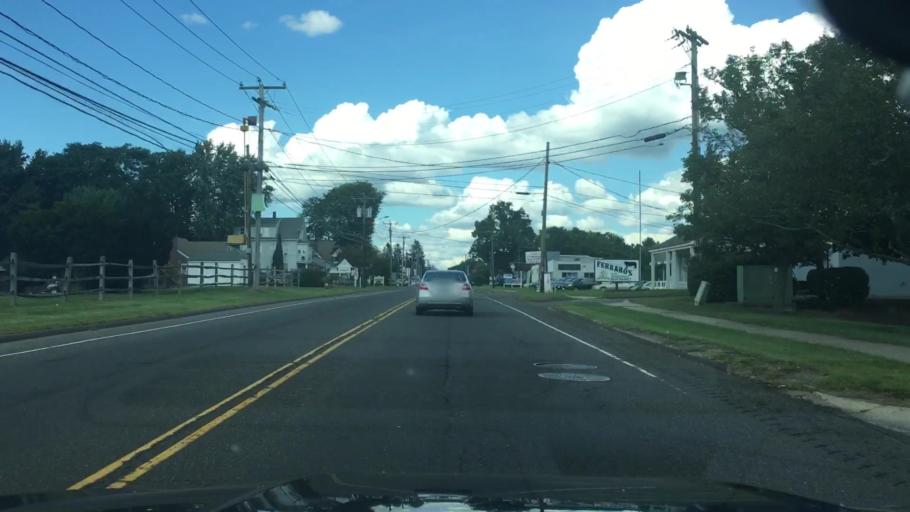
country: US
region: Connecticut
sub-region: New Haven County
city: Meriden
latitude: 41.5161
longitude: -72.8046
